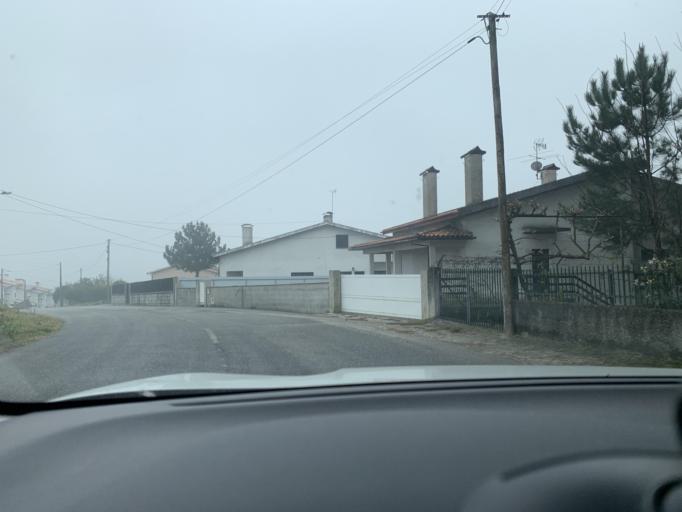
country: PT
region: Viseu
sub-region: Viseu
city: Viseu
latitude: 40.6270
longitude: -7.9177
